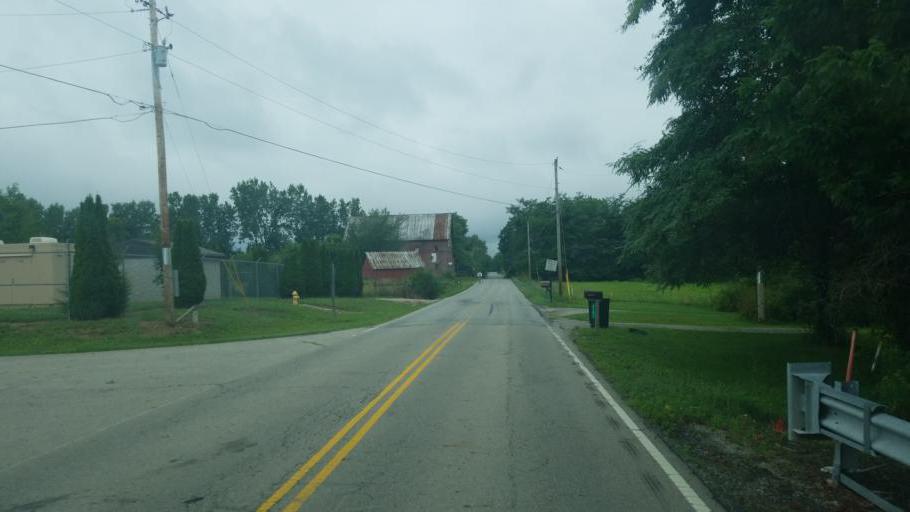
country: US
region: Ohio
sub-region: Delaware County
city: Sunbury
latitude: 40.3023
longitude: -82.8670
